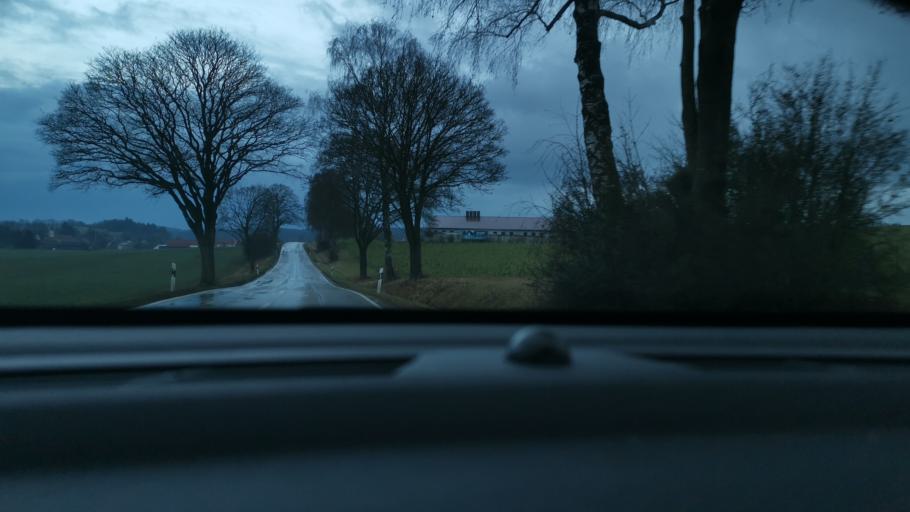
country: DE
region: Bavaria
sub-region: Swabia
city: Aindling
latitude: 48.5648
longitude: 10.9805
